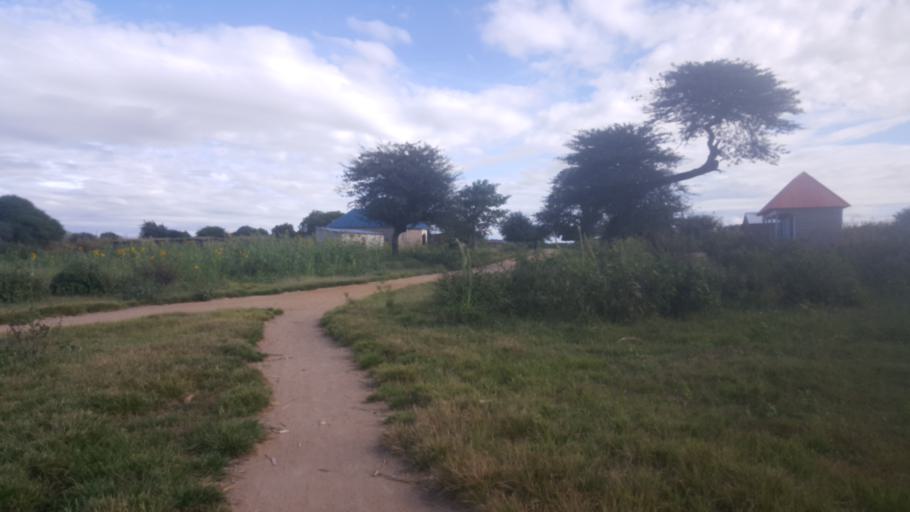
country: TZ
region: Dodoma
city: Dodoma
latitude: -6.0963
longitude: 35.5286
